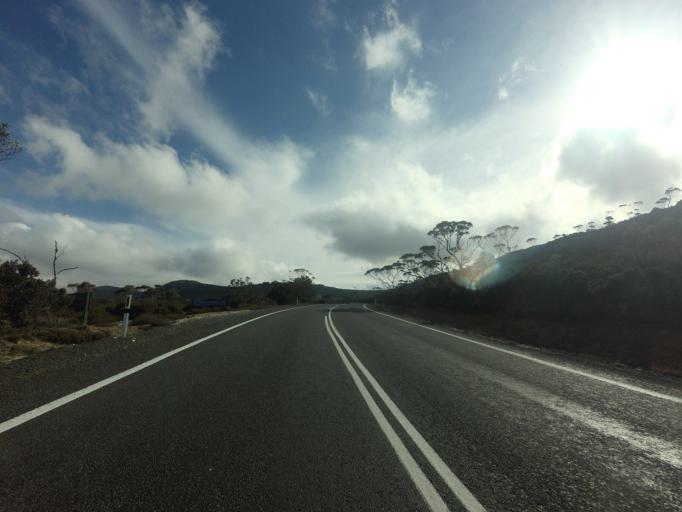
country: AU
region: Tasmania
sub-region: Meander Valley
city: Deloraine
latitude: -41.7306
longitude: 146.7135
